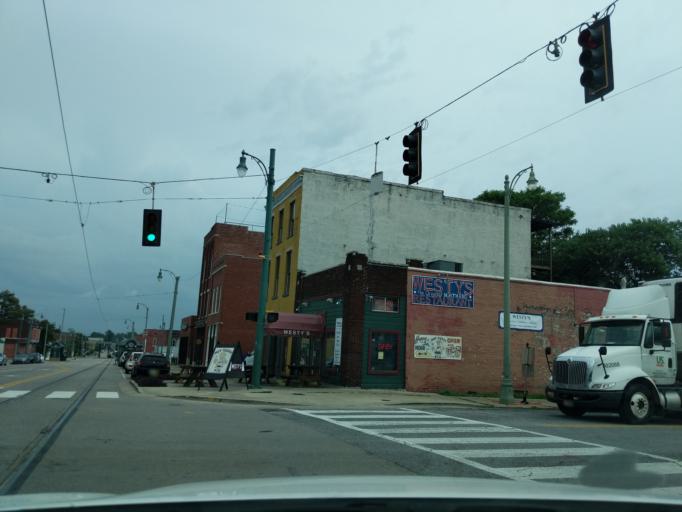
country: US
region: Tennessee
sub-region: Shelby County
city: Memphis
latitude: 35.1540
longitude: -90.0492
